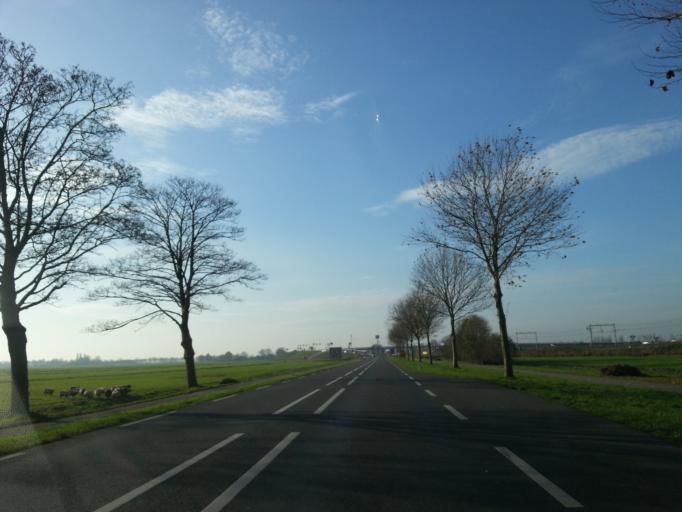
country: NL
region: South Holland
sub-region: Gemeente Gouda
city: Bloemendaal
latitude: 52.0064
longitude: 4.6618
